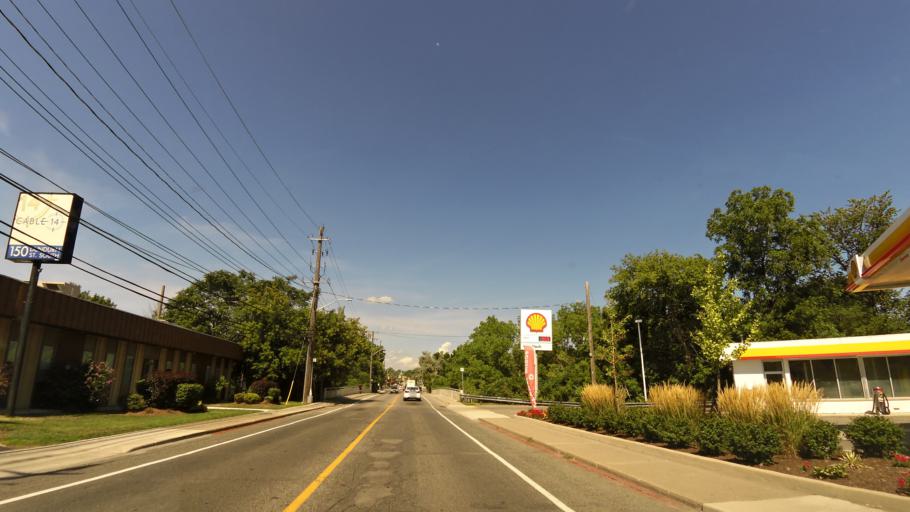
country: CA
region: Ontario
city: Hamilton
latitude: 43.2572
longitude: -79.8898
